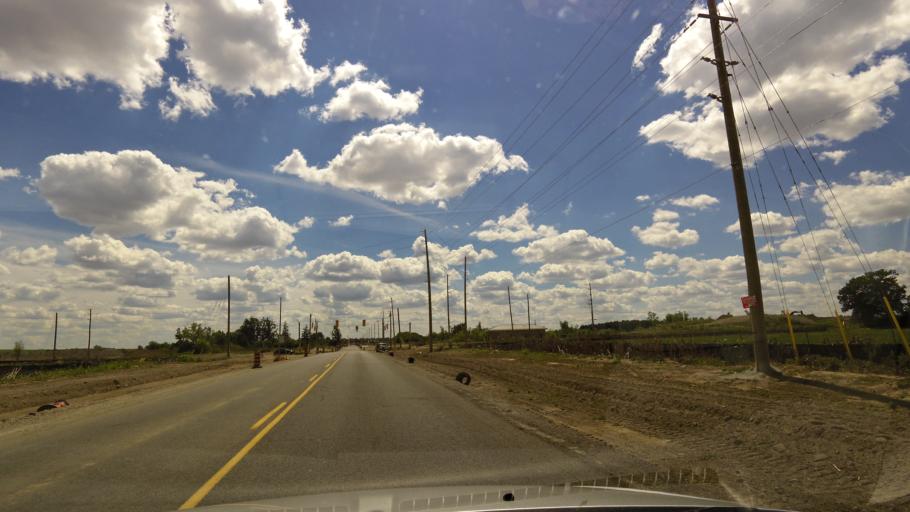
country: CA
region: Ontario
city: Brampton
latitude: 43.6387
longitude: -79.8618
